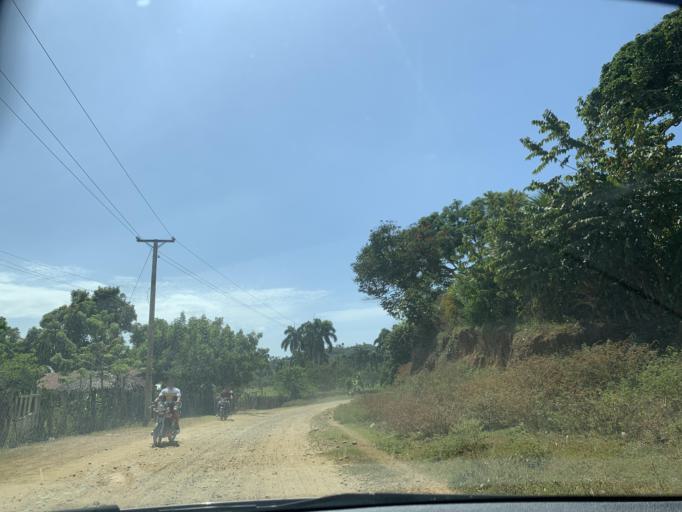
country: DO
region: Puerto Plata
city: Luperon
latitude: 19.8832
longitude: -70.8712
